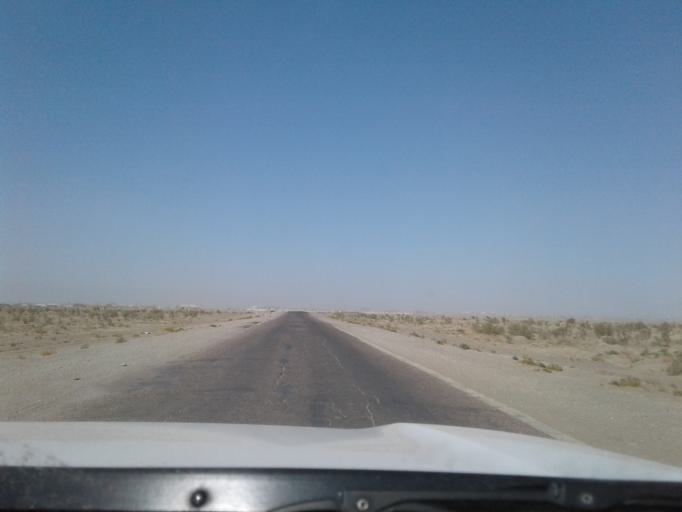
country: TM
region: Balkan
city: Gumdag
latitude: 39.1806
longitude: 54.5828
